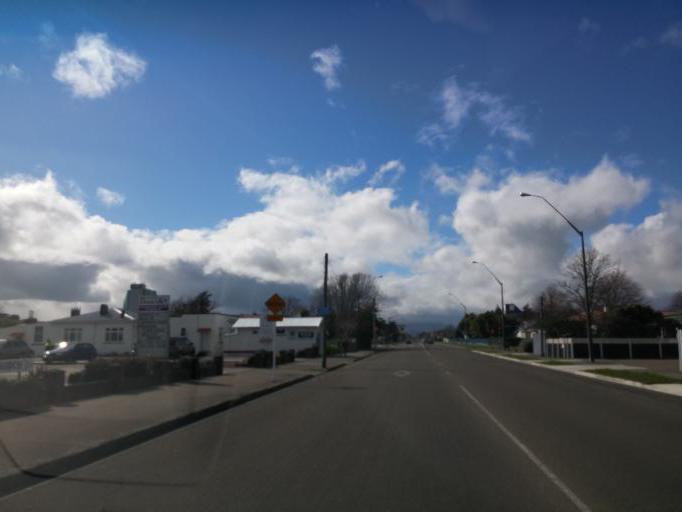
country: NZ
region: Manawatu-Wanganui
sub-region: Palmerston North City
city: Palmerston North
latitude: -40.3618
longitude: 175.6080
